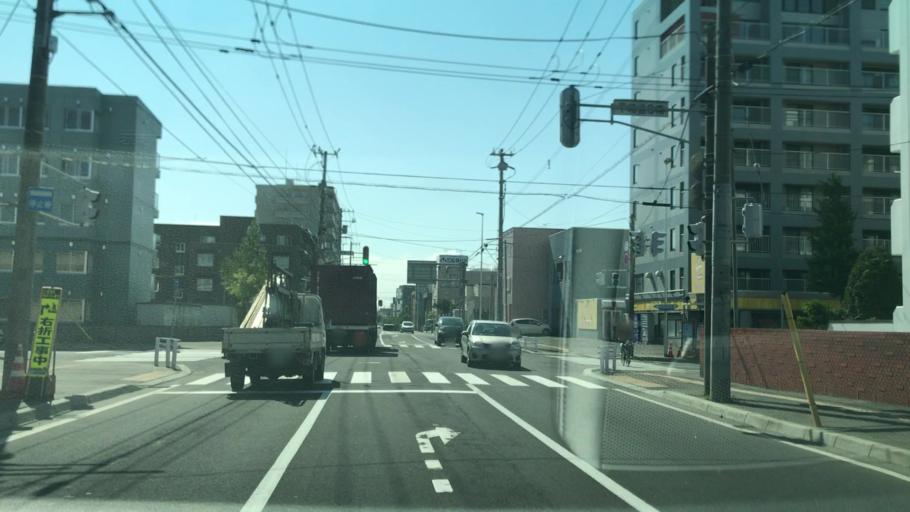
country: JP
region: Hokkaido
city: Sapporo
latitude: 43.0520
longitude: 141.4116
